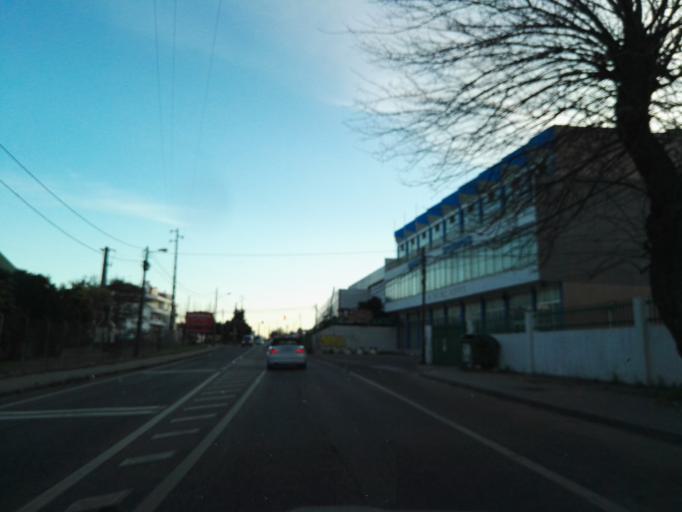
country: PT
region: Lisbon
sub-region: Loures
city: Santa Iria da Azoia
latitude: 38.8429
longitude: -9.0809
